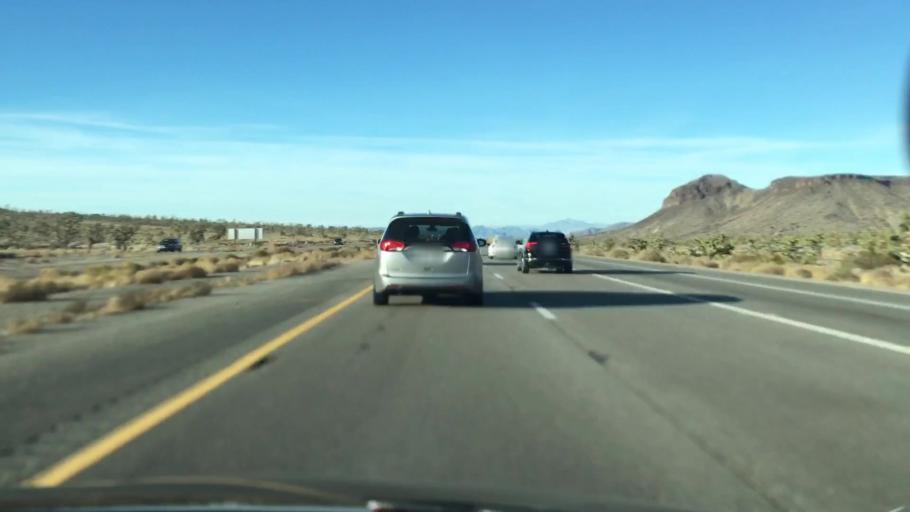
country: US
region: Nevada
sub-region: Clark County
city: Sandy Valley
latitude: 35.3985
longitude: -115.8077
